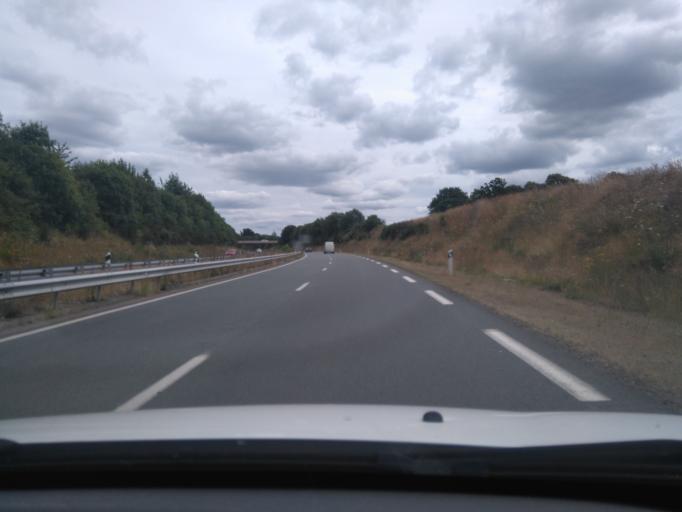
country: FR
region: Brittany
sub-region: Departement des Cotes-d'Armor
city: Begard
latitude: 48.6253
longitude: -3.3195
